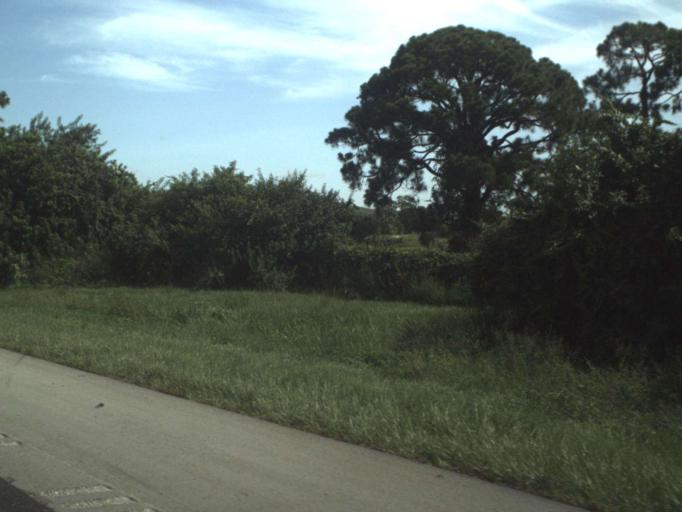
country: US
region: Florida
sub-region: Indian River County
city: West Vero Corridor
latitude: 27.5686
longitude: -80.4890
